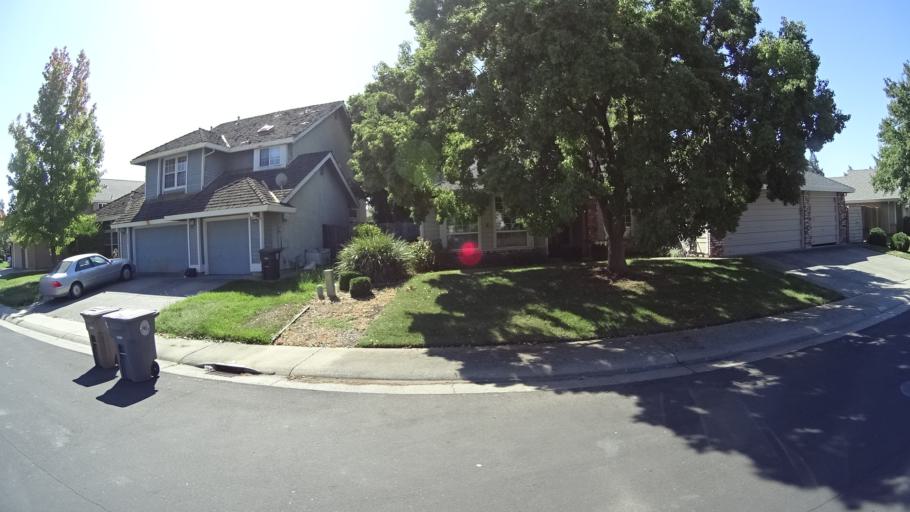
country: US
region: California
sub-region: Sacramento County
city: Laguna
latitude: 38.4271
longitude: -121.4360
